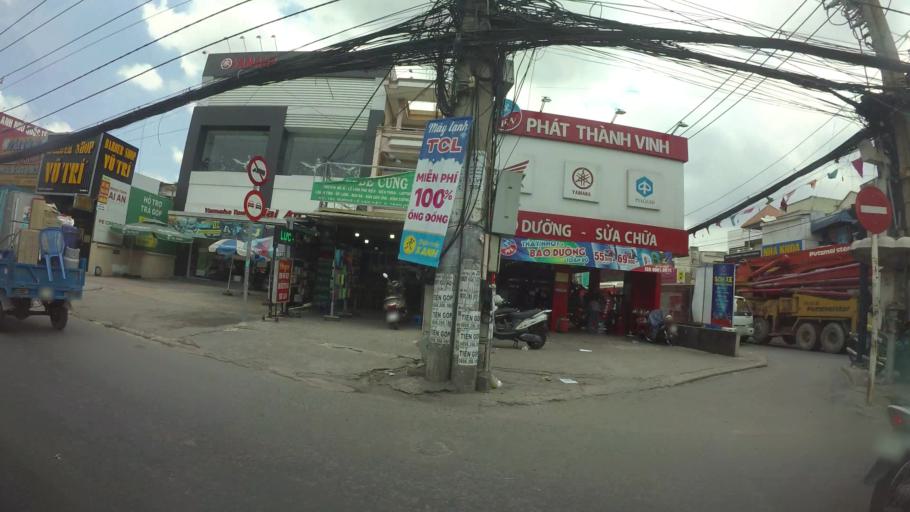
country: VN
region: Ho Chi Minh City
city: Thu Duc
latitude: 10.8430
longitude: 106.7811
